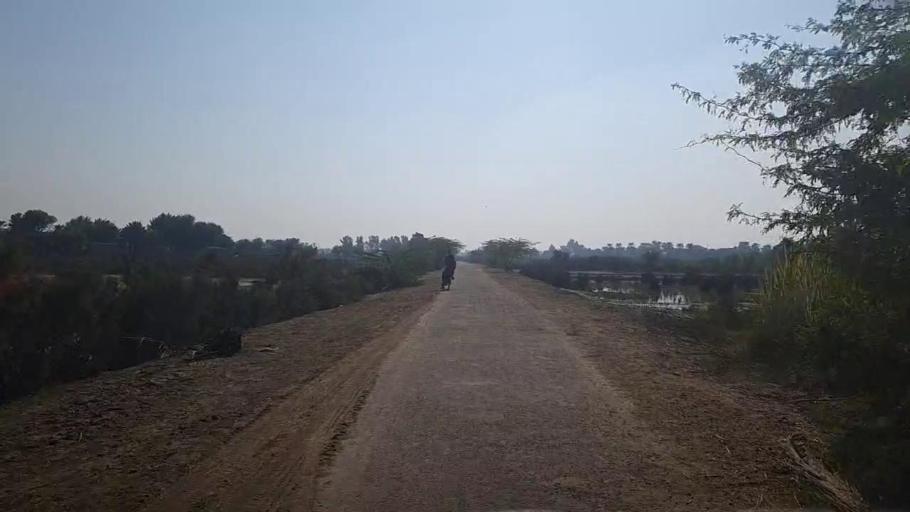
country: PK
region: Sindh
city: Kot Diji
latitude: 27.4276
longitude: 68.7371
